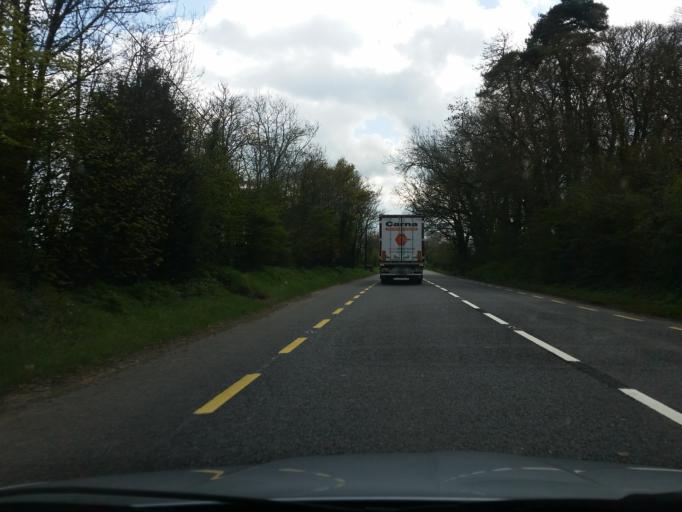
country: IE
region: Leinster
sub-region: An Mhi
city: Ashbourne
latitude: 53.5464
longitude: -6.4315
